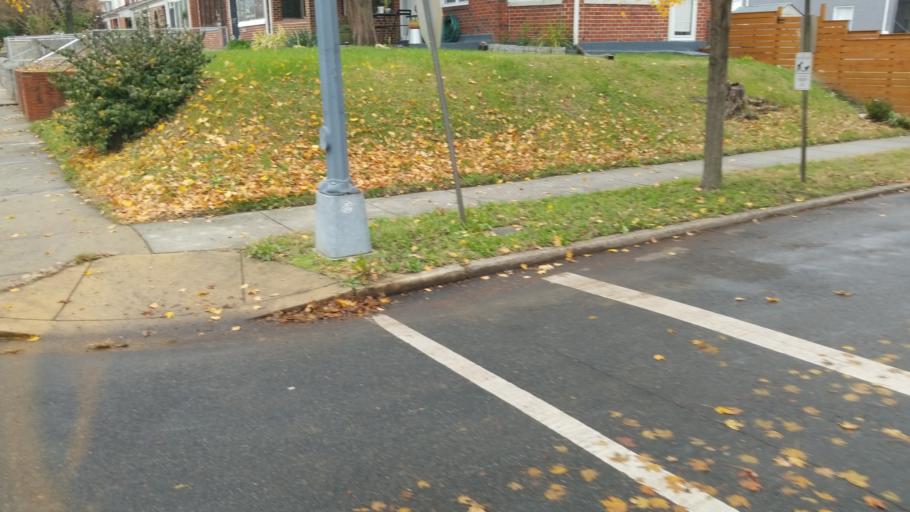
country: US
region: Maryland
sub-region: Prince George's County
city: Colmar Manor
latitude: 38.8936
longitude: -76.9576
